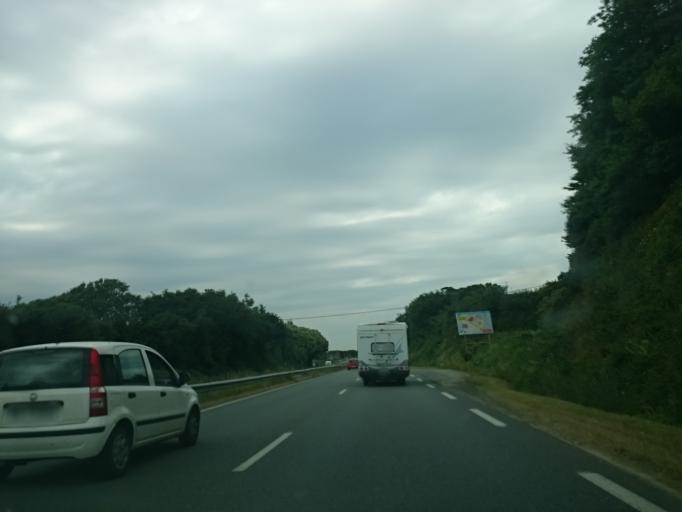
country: FR
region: Brittany
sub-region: Departement du Finistere
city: Guilers
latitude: 48.4218
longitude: -4.5656
